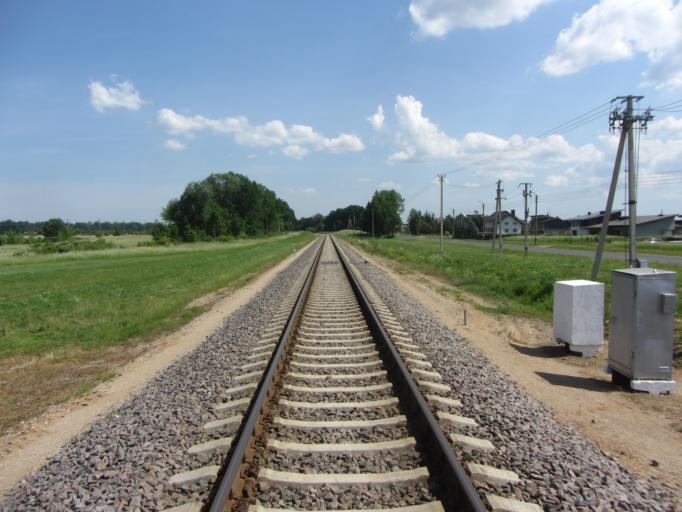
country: LT
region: Kauno apskritis
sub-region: Kauno rajonas
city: Karmelava
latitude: 54.9304
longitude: 24.0931
